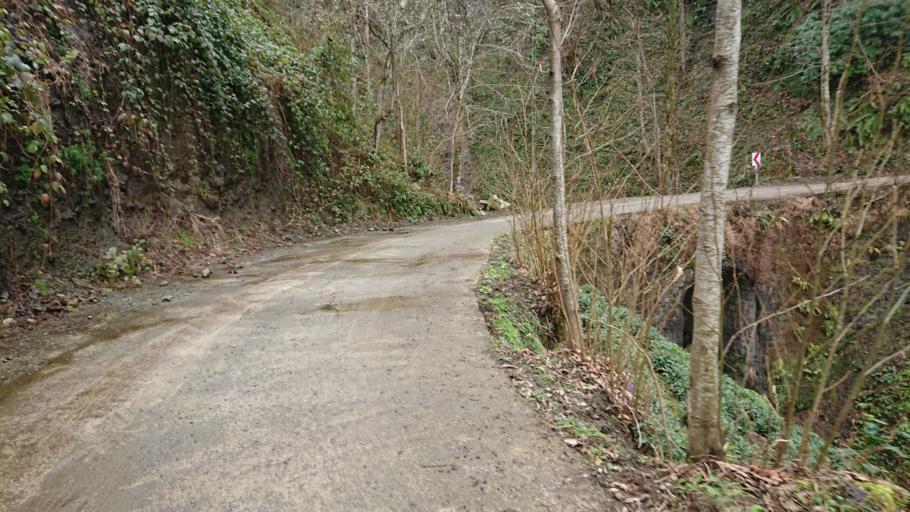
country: TR
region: Rize
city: Rize
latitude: 40.9770
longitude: 40.4964
